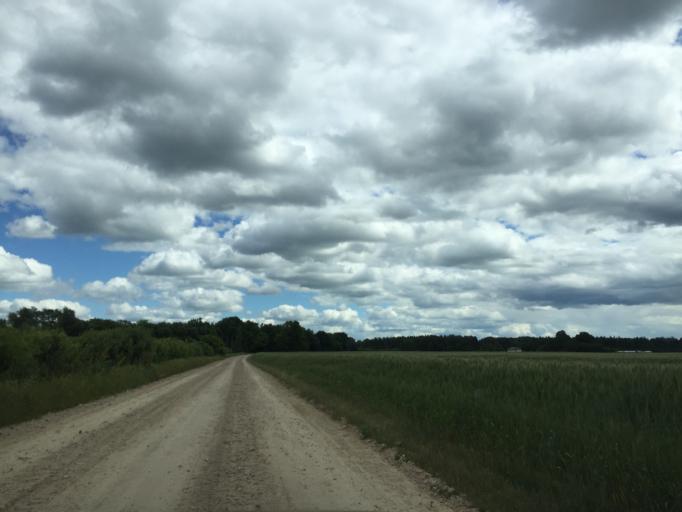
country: LV
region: Lecava
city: Iecava
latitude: 56.5885
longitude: 24.2469
